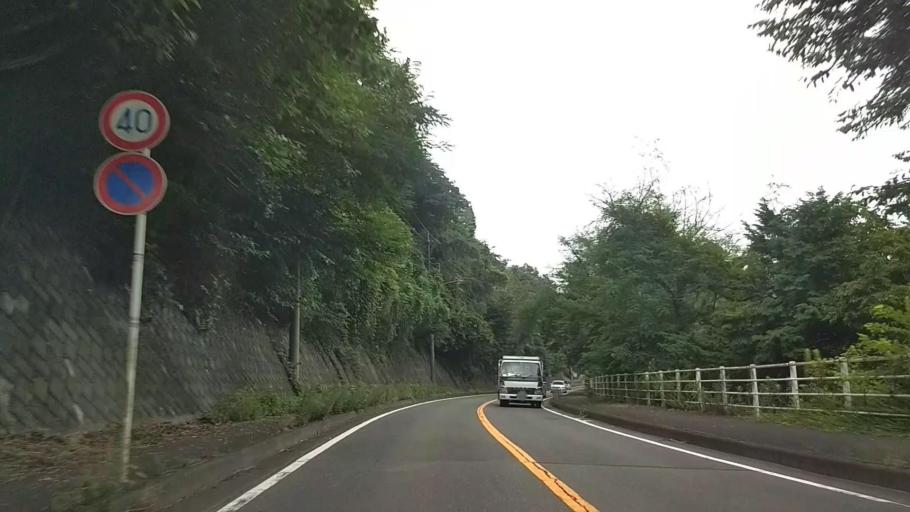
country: JP
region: Kanagawa
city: Hadano
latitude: 35.3399
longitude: 139.2220
